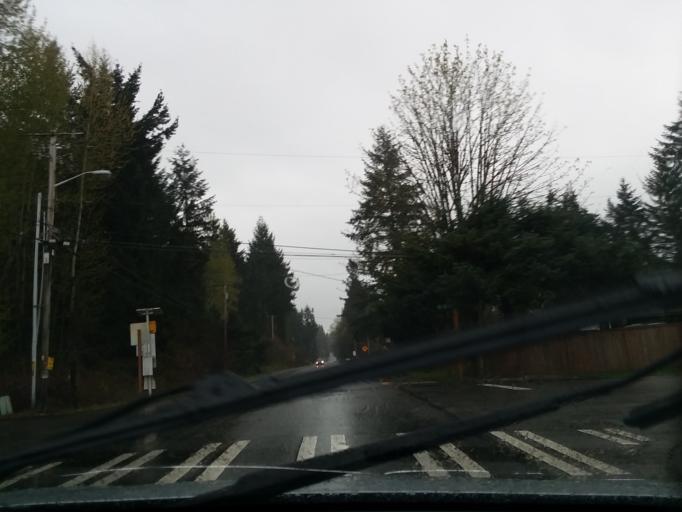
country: US
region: Washington
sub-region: King County
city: Fairwood
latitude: 47.4814
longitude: -122.1483
